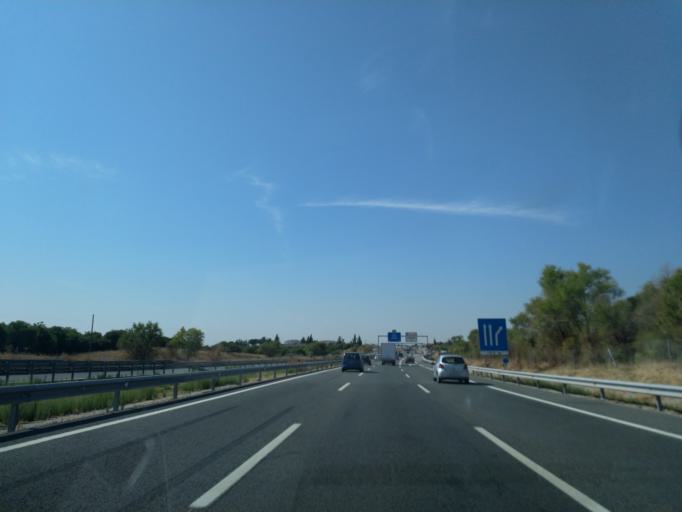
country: ES
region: Madrid
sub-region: Provincia de Madrid
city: Navalcarnero
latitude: 40.2558
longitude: -4.0490
